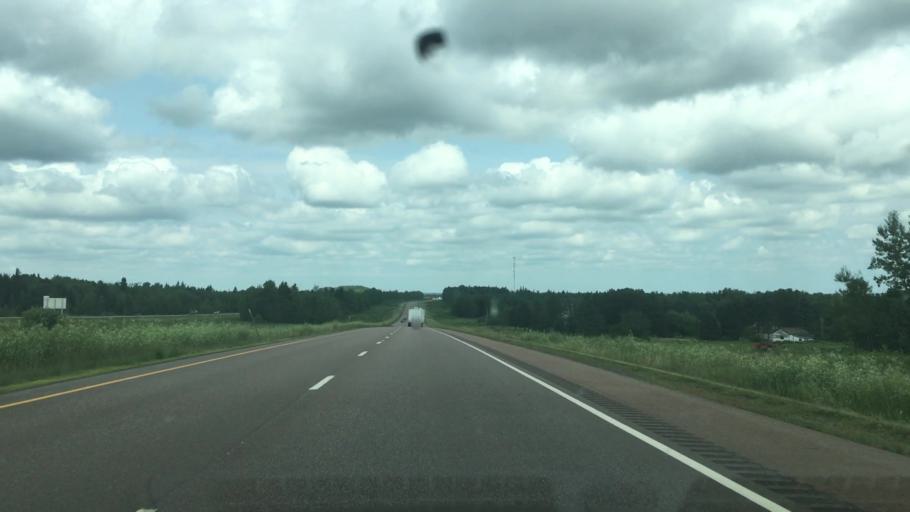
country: CA
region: New Brunswick
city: Dieppe
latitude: 46.0670
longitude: -64.5890
